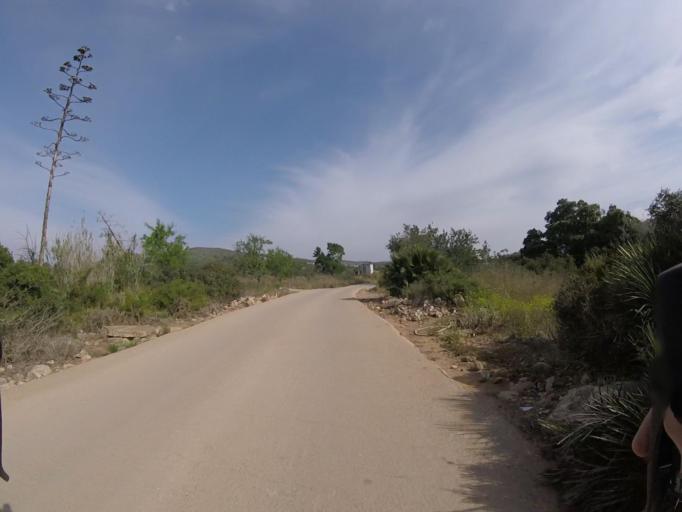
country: ES
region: Valencia
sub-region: Provincia de Castello
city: Alcala de Xivert
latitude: 40.2697
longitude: 0.2525
